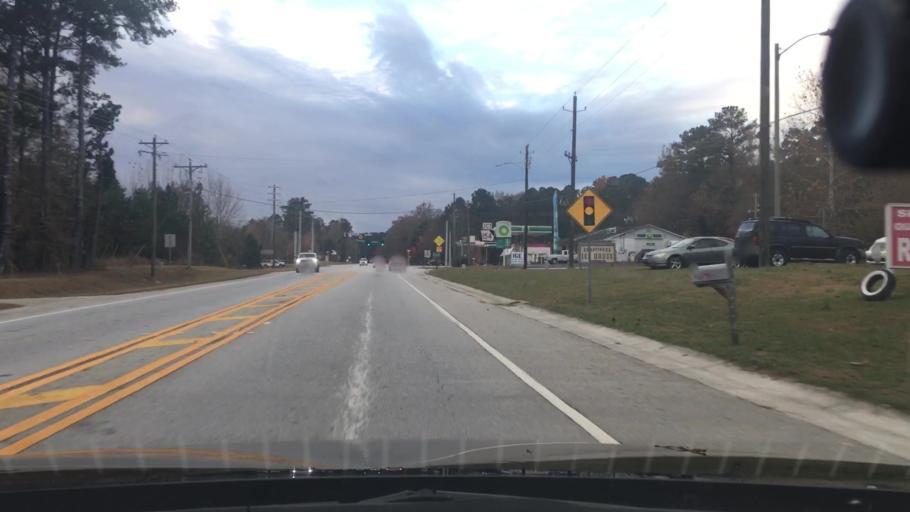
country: US
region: Georgia
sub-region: Fayette County
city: Peachtree City
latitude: 33.3432
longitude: -84.6448
